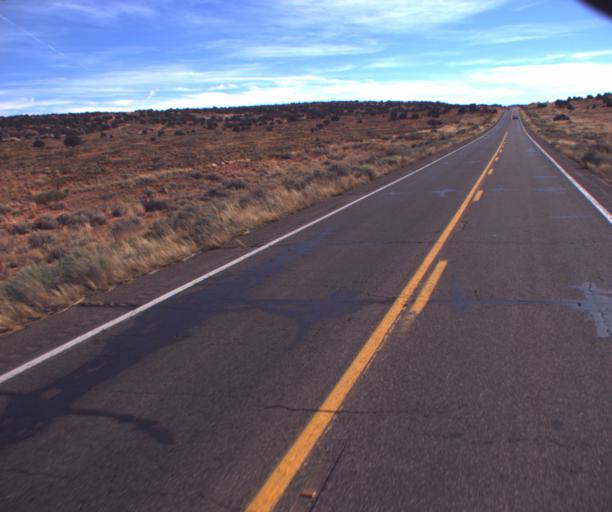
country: US
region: Arizona
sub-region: Coconino County
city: Kaibito
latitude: 36.5808
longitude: -111.1422
